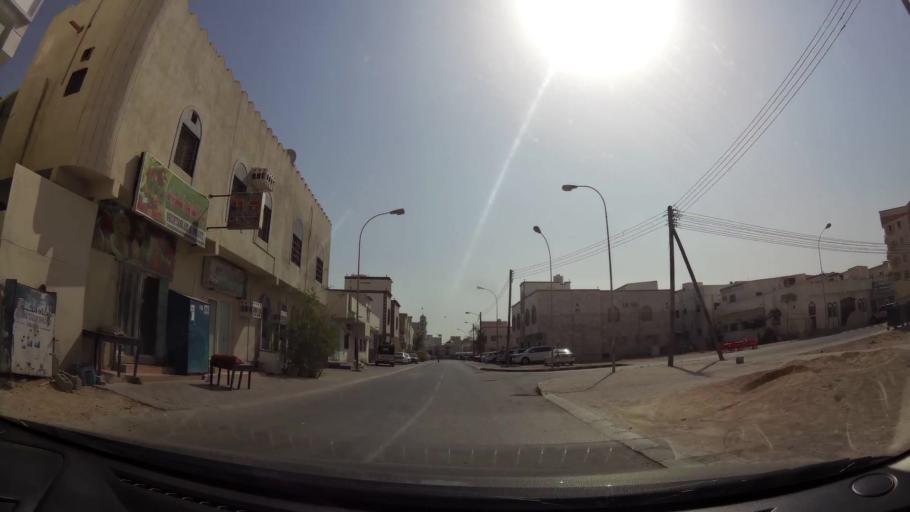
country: OM
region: Zufar
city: Salalah
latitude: 17.0031
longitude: 54.0493
